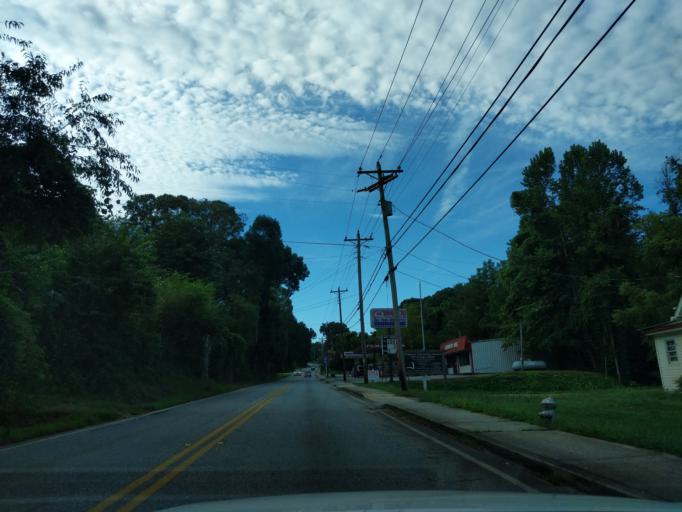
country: US
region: Georgia
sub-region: Fannin County
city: McCaysville
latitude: 34.9819
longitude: -84.3744
